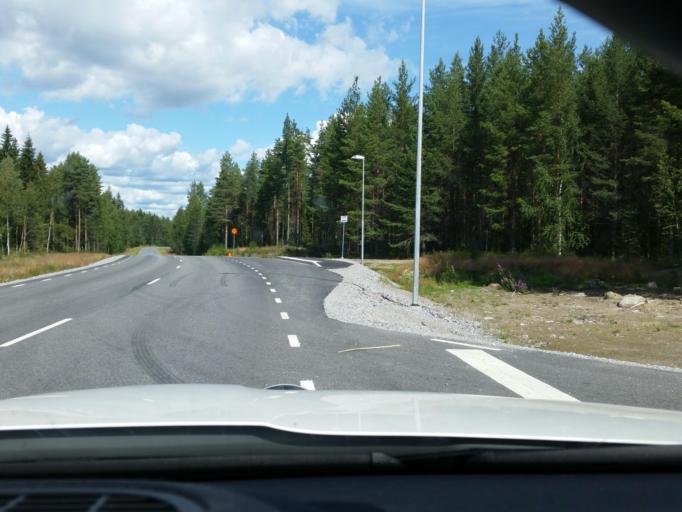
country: SE
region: Norrbotten
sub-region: Pitea Kommun
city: Norrfjarden
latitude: 65.4048
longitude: 21.4620
